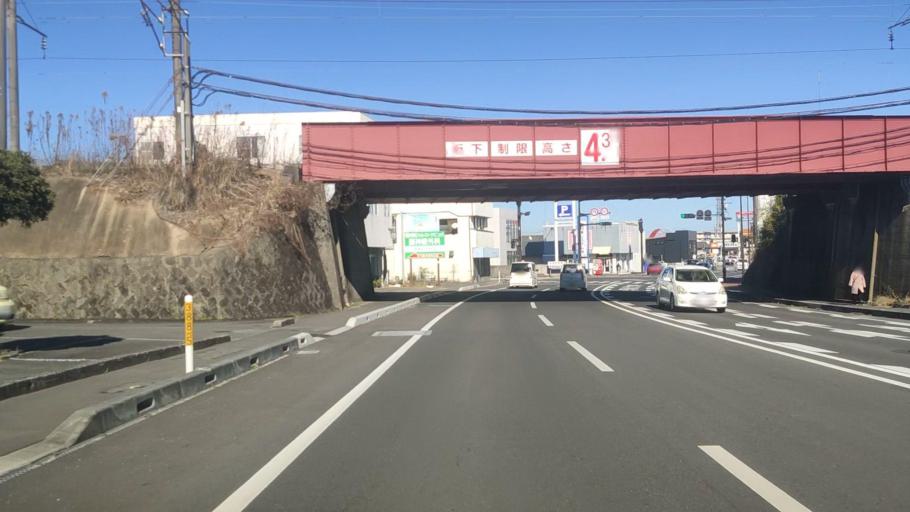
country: JP
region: Miyazaki
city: Miyakonojo
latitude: 31.7368
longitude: 131.0692
